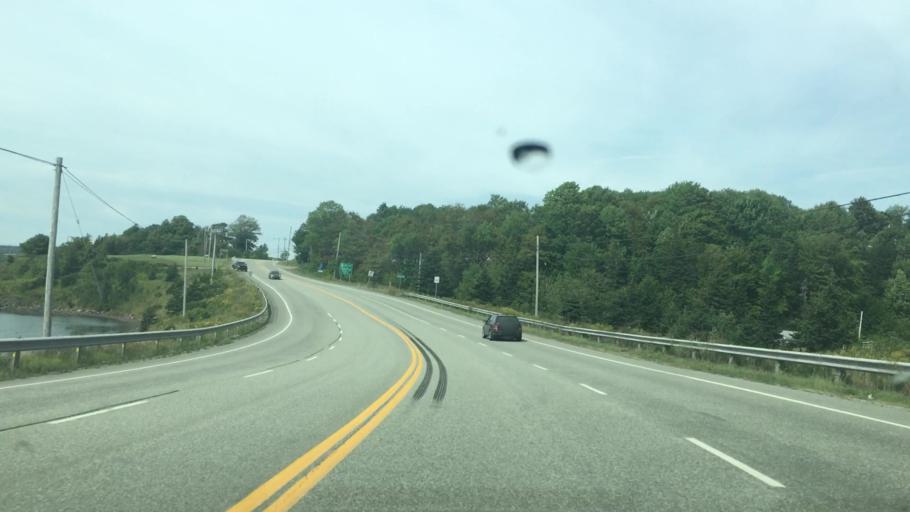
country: CA
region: Nova Scotia
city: Port Hawkesbury
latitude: 45.6442
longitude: -61.3964
